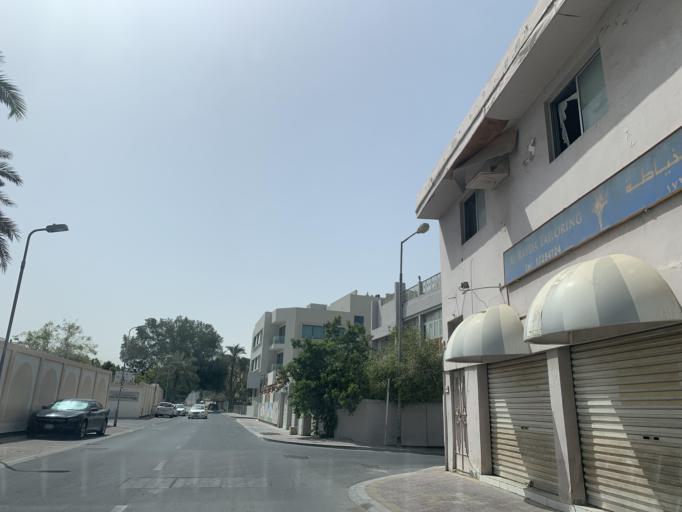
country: BH
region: Manama
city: Jidd Hafs
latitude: 26.2179
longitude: 50.5609
